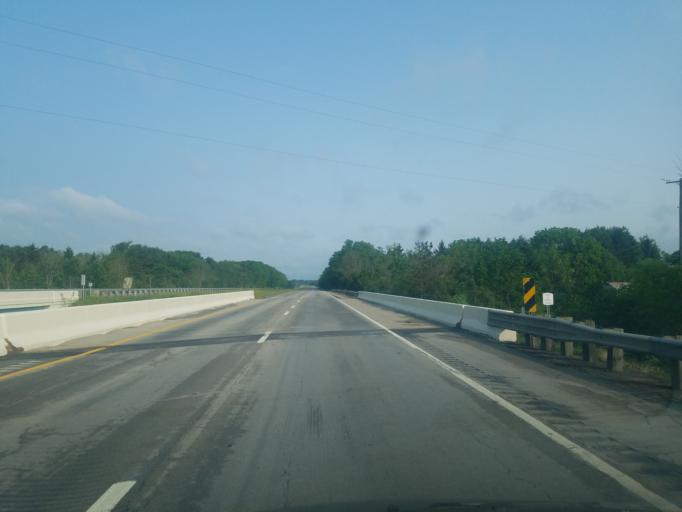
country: US
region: Ohio
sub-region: Stark County
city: Brewster
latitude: 40.7791
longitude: -81.6032
